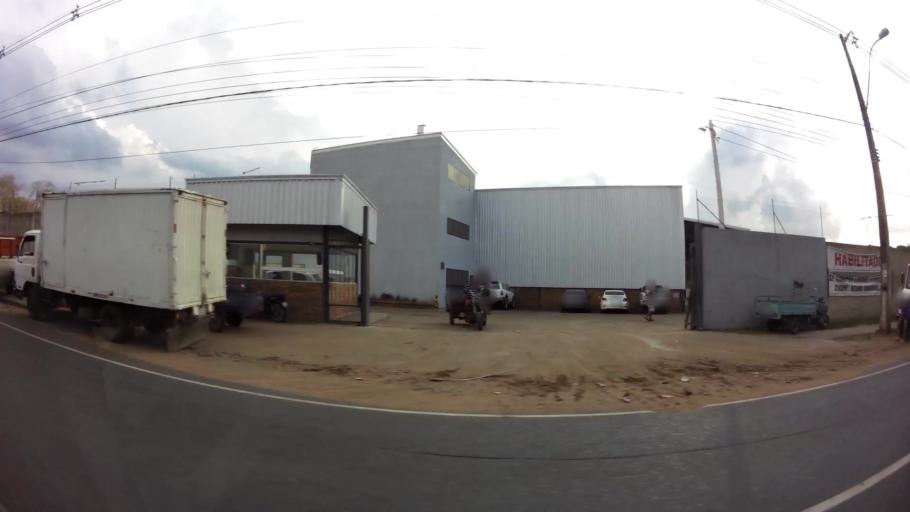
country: PY
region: Central
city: Villa Elisa
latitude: -25.3616
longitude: -57.5664
